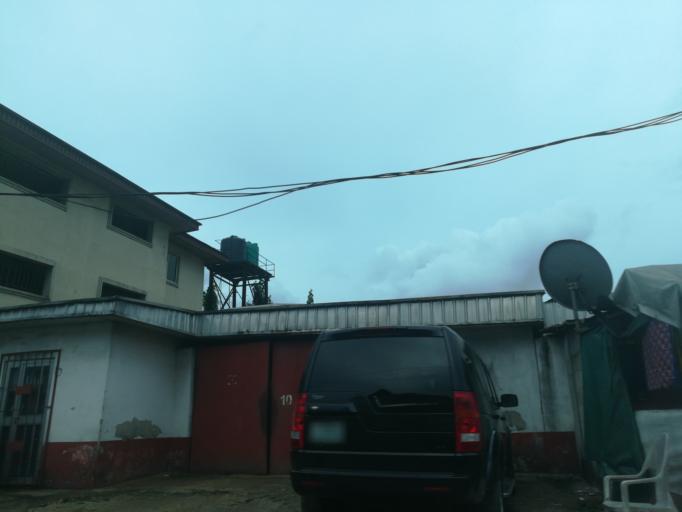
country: NG
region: Rivers
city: Port Harcourt
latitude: 4.8134
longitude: 6.9893
